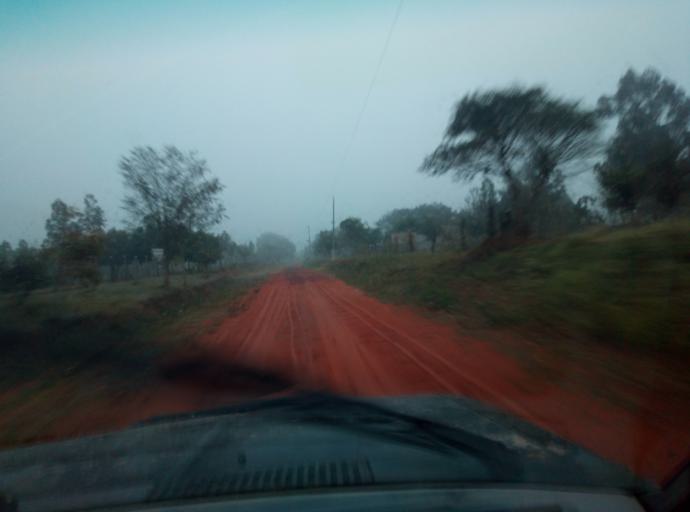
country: PY
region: Caaguazu
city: Doctor Cecilio Baez
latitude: -25.1550
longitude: -56.2881
